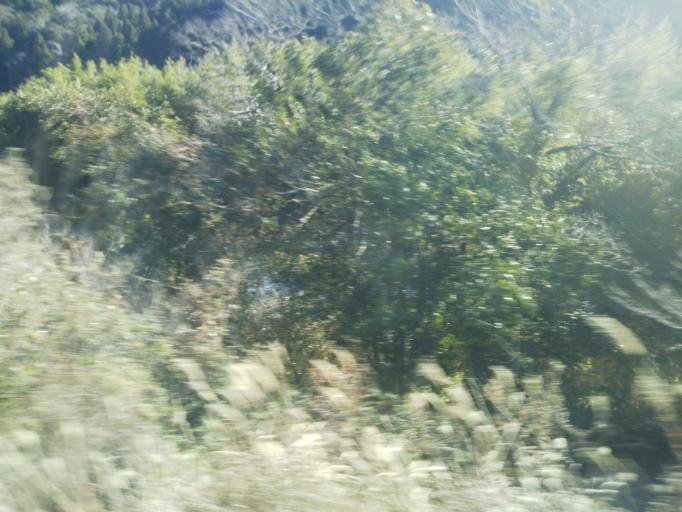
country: JP
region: Kochi
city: Nakamura
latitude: 33.1093
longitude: 133.1002
